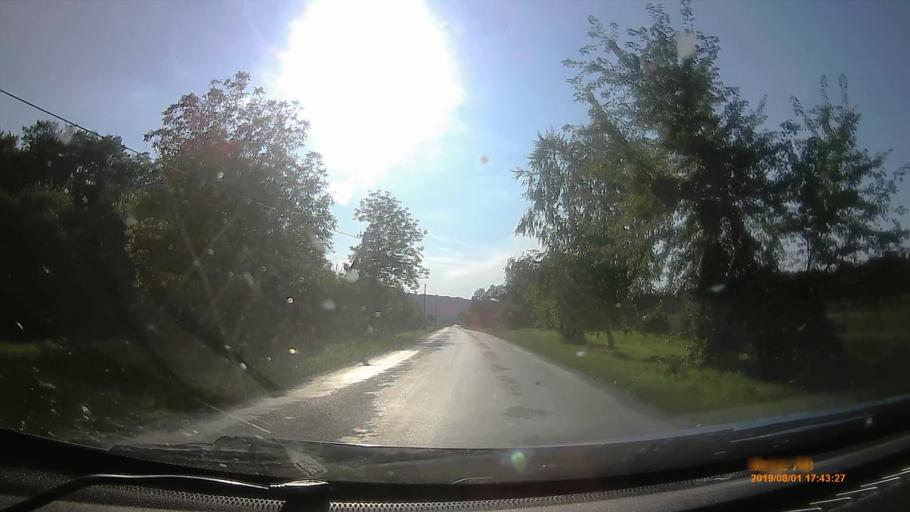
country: HU
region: Baranya
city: Sasd
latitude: 46.1923
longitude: 18.1499
